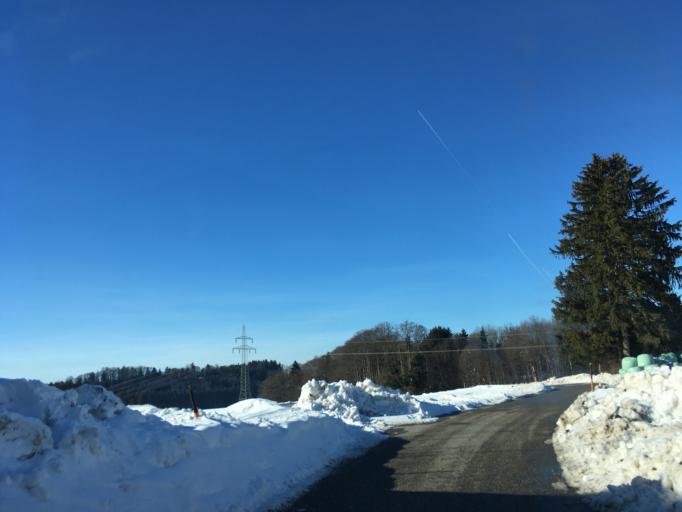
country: DE
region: Bavaria
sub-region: Upper Bavaria
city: Aschau im Chiemgau
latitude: 47.8144
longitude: 12.3339
